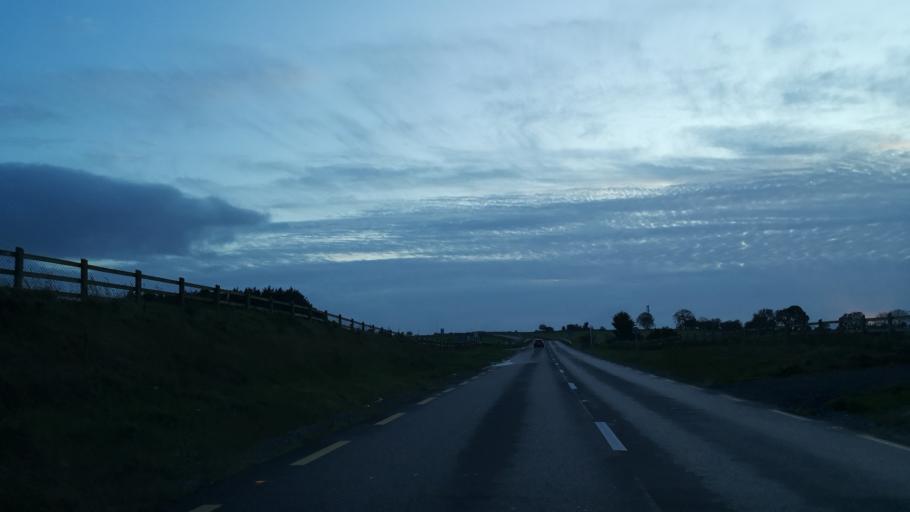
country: IE
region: Connaught
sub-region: County Galway
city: Tuam
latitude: 53.4076
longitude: -8.8094
